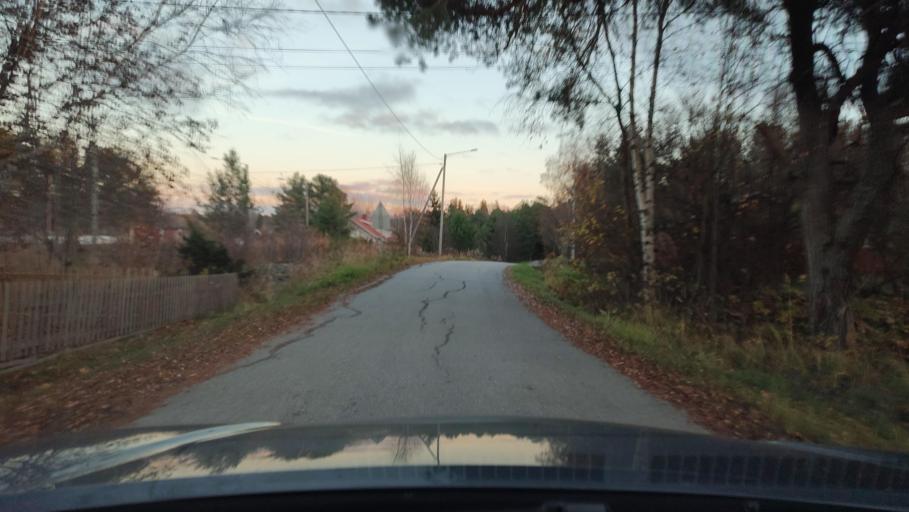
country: FI
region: Ostrobothnia
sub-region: Sydosterbotten
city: Kristinestad
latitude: 62.2987
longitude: 21.4588
